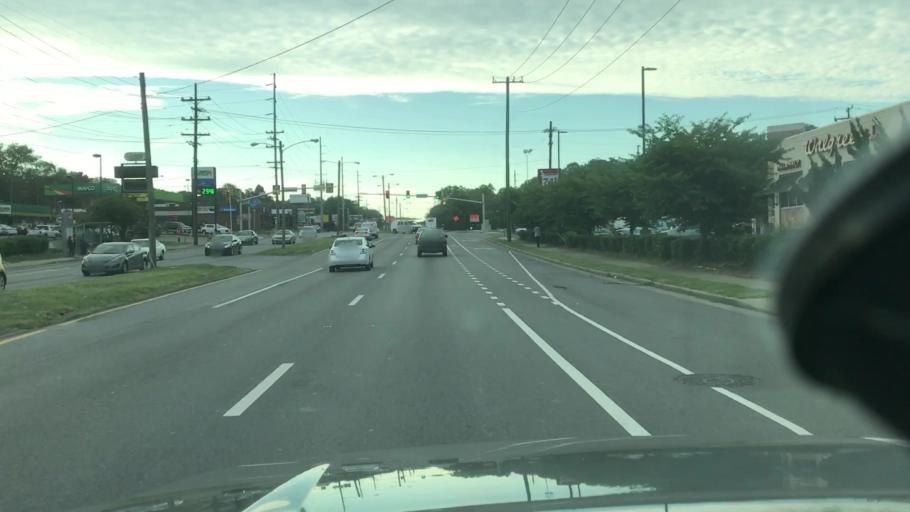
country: US
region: Tennessee
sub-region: Davidson County
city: Oak Hill
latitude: 36.1274
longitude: -86.7121
